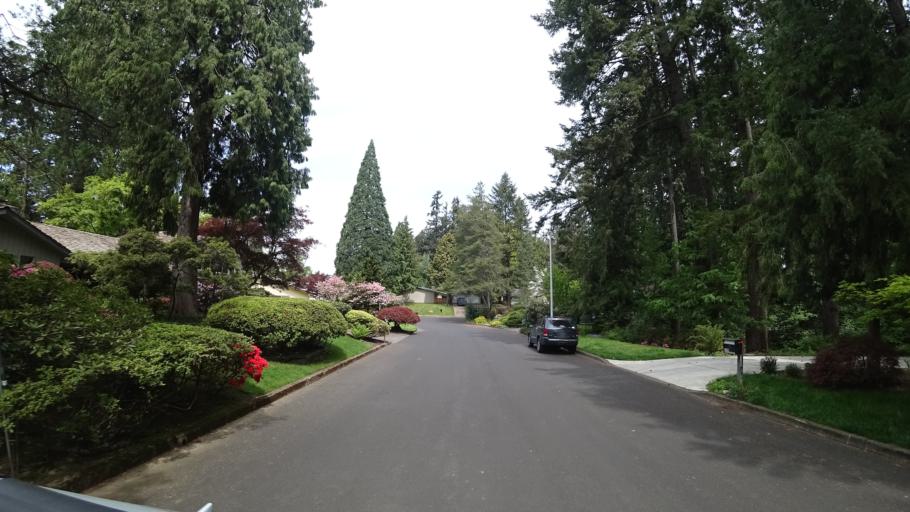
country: US
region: Oregon
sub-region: Washington County
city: Hillsboro
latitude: 45.5098
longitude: -122.9436
